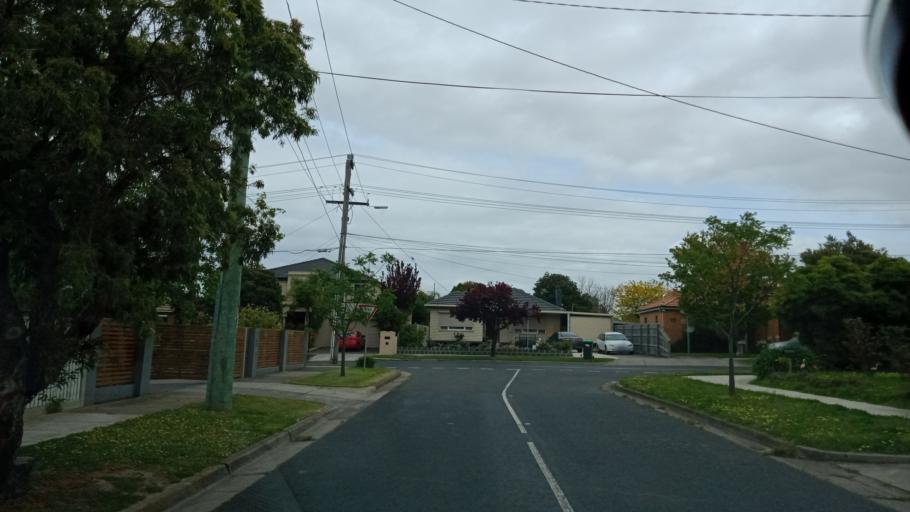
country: AU
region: Victoria
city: McKinnon
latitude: -37.9191
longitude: 145.0669
